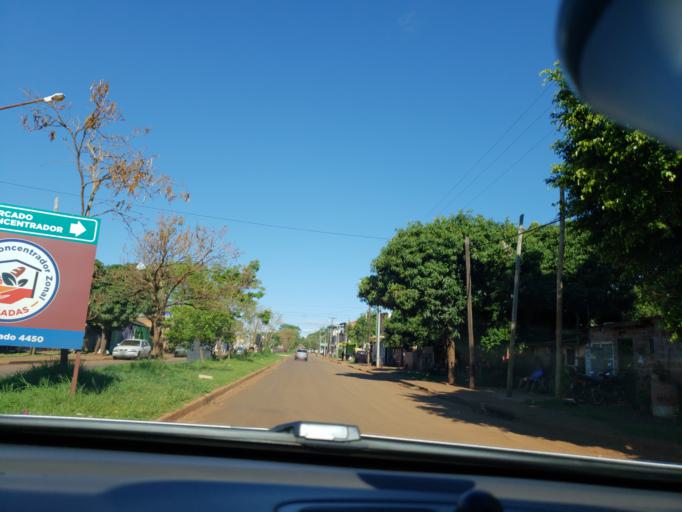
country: AR
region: Misiones
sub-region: Departamento de Capital
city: Posadas
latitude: -27.3846
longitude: -55.9275
